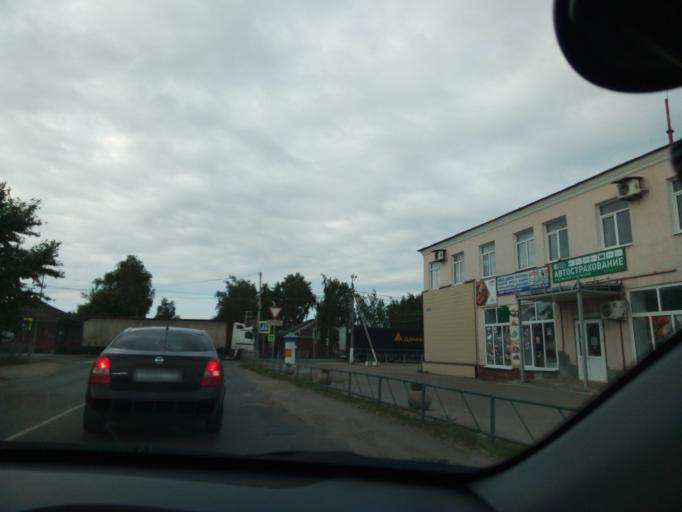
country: RU
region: Rjazan
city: Shatsk
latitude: 54.0259
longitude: 41.7122
